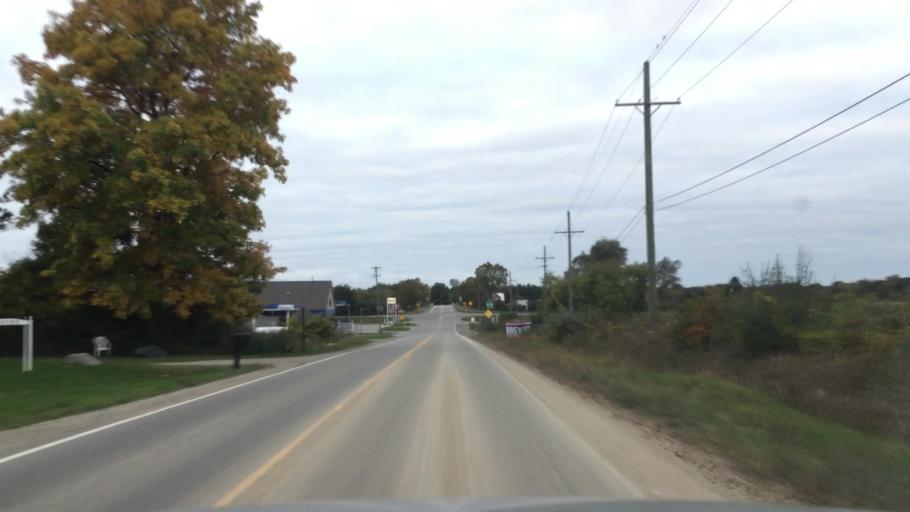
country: US
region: Michigan
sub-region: Genesee County
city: Fenton
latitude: 42.6769
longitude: -83.7551
